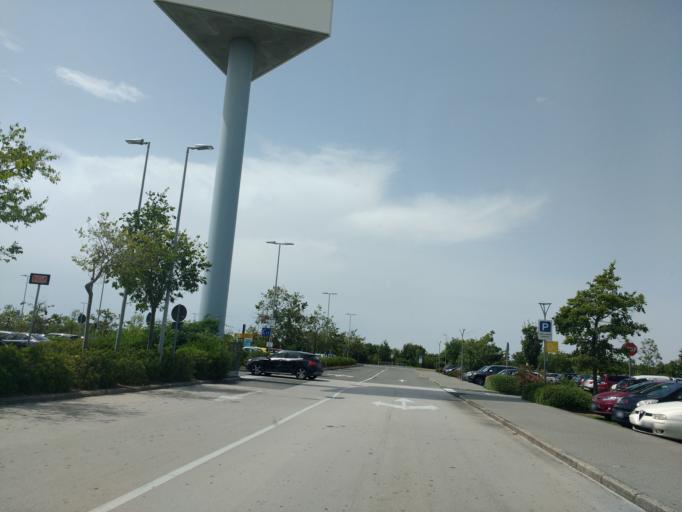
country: IT
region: Latium
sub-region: Citta metropolitana di Roma Capitale
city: Selcetta
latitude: 41.7188
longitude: 12.4453
